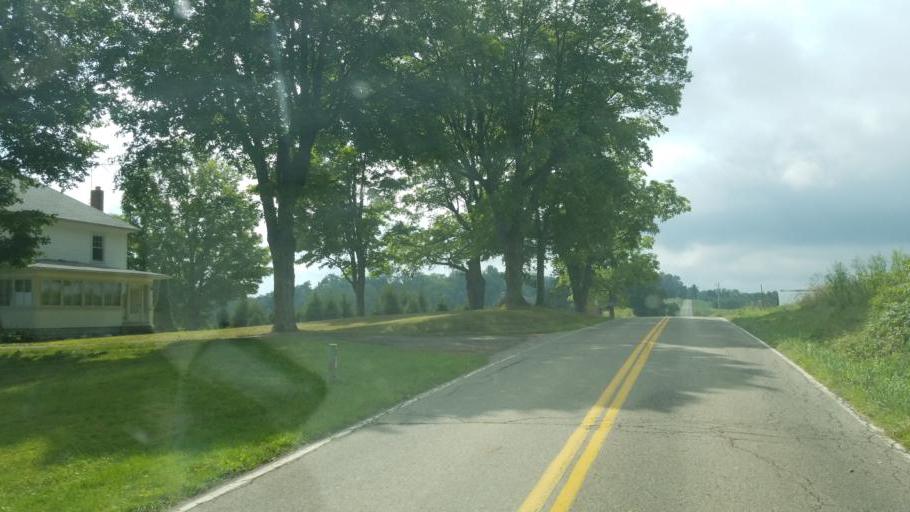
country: US
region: Ohio
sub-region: Licking County
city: Utica
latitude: 40.2186
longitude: -82.4584
